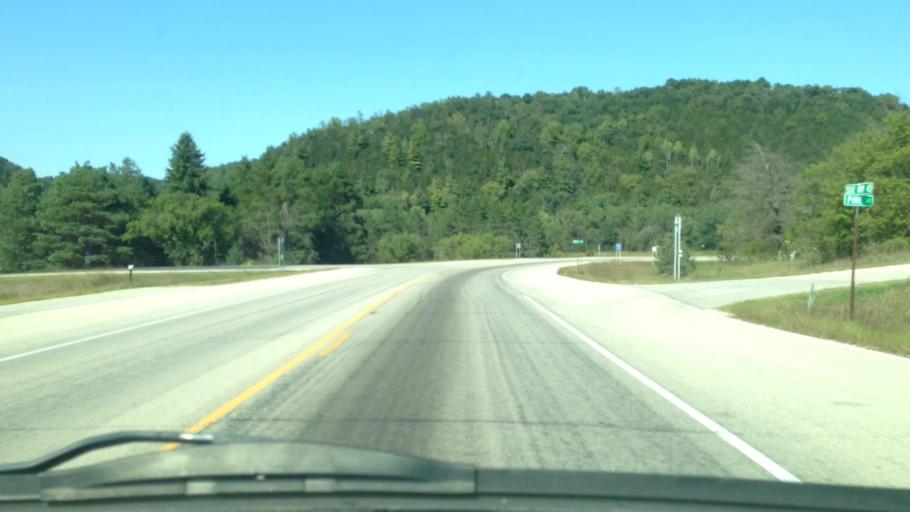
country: US
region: Minnesota
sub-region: Fillmore County
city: Rushford
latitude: 43.8326
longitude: -91.7655
